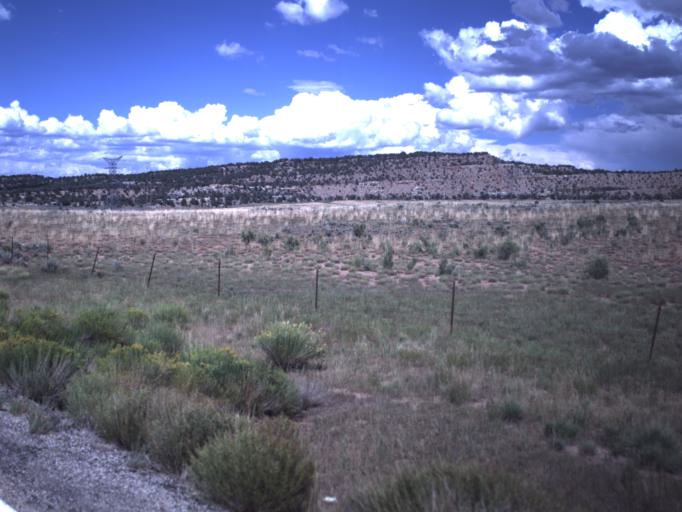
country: US
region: Utah
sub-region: Duchesne County
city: Duchesne
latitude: 40.2166
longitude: -110.7265
